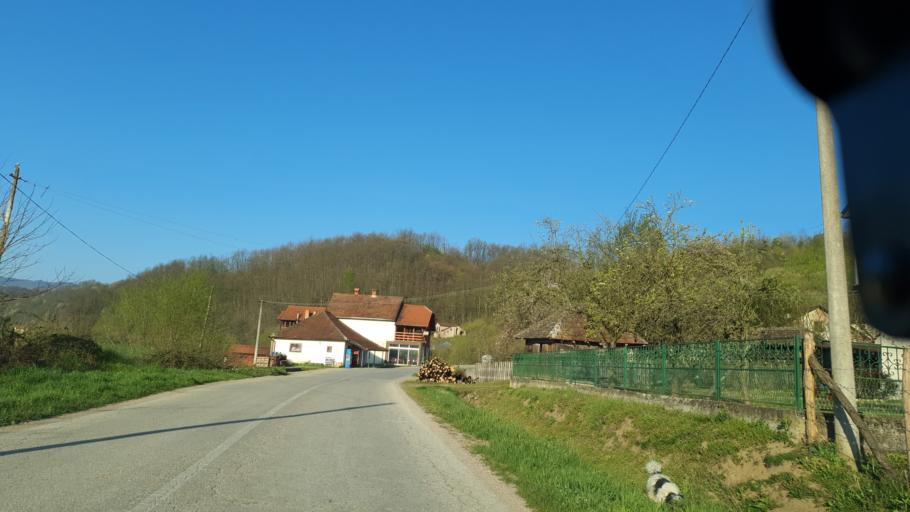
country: RS
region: Central Serbia
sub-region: Kolubarski Okrug
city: Osecina
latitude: 44.3561
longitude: 19.5283
